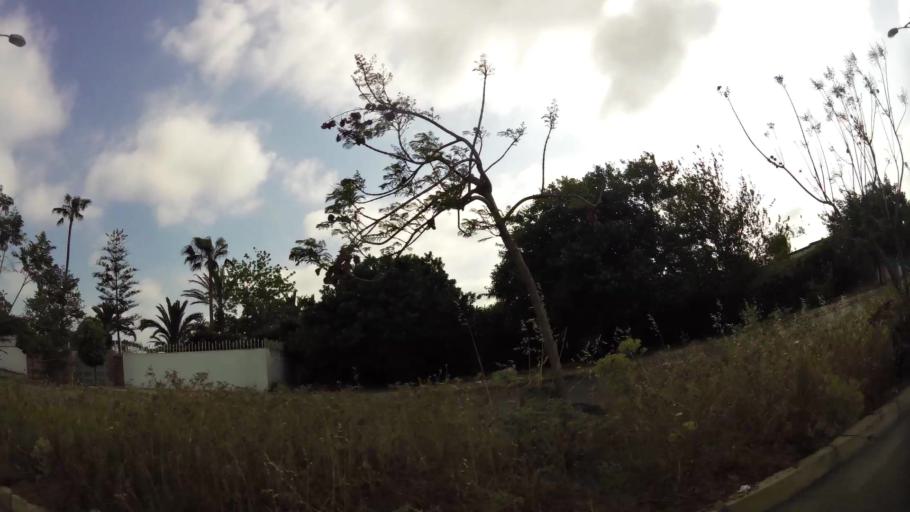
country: MA
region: Rabat-Sale-Zemmour-Zaer
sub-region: Rabat
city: Rabat
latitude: 33.9701
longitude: -6.8504
